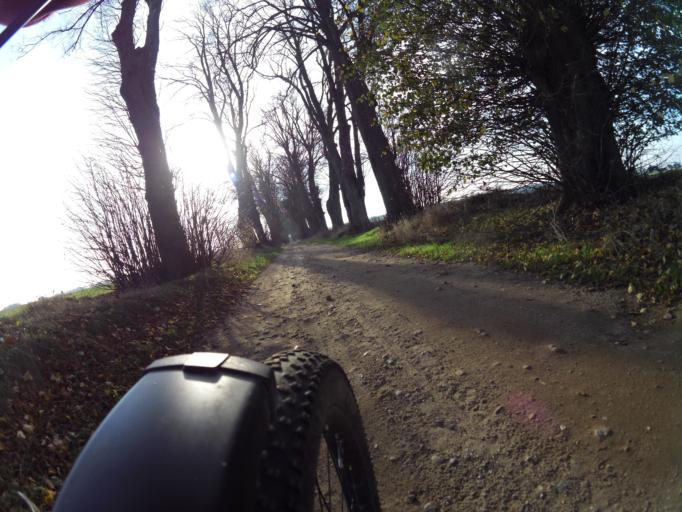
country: PL
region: Pomeranian Voivodeship
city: Strzelno
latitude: 54.7555
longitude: 18.2913
